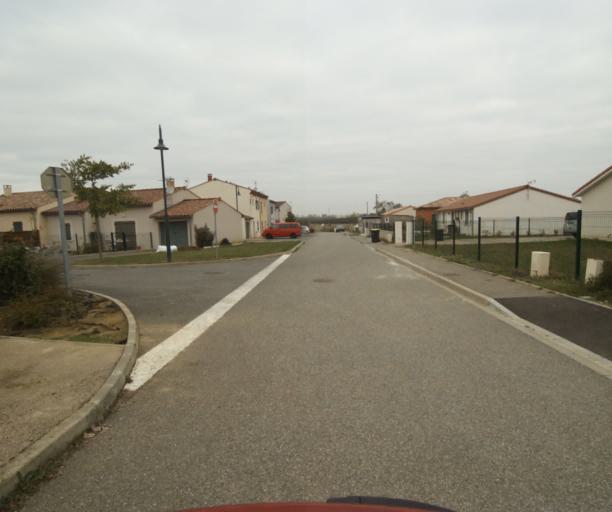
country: FR
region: Midi-Pyrenees
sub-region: Departement du Tarn-et-Garonne
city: Verdun-sur-Garonne
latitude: 43.8033
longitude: 1.2196
